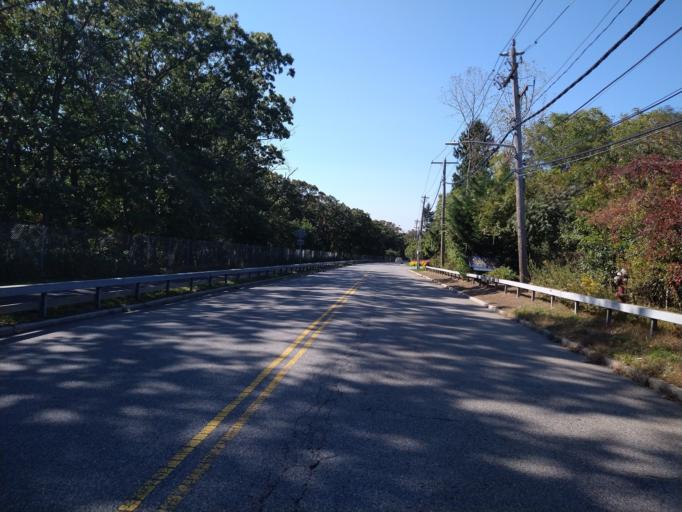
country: US
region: New York
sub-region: Nassau County
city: Plainview
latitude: 40.7993
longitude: -73.4716
